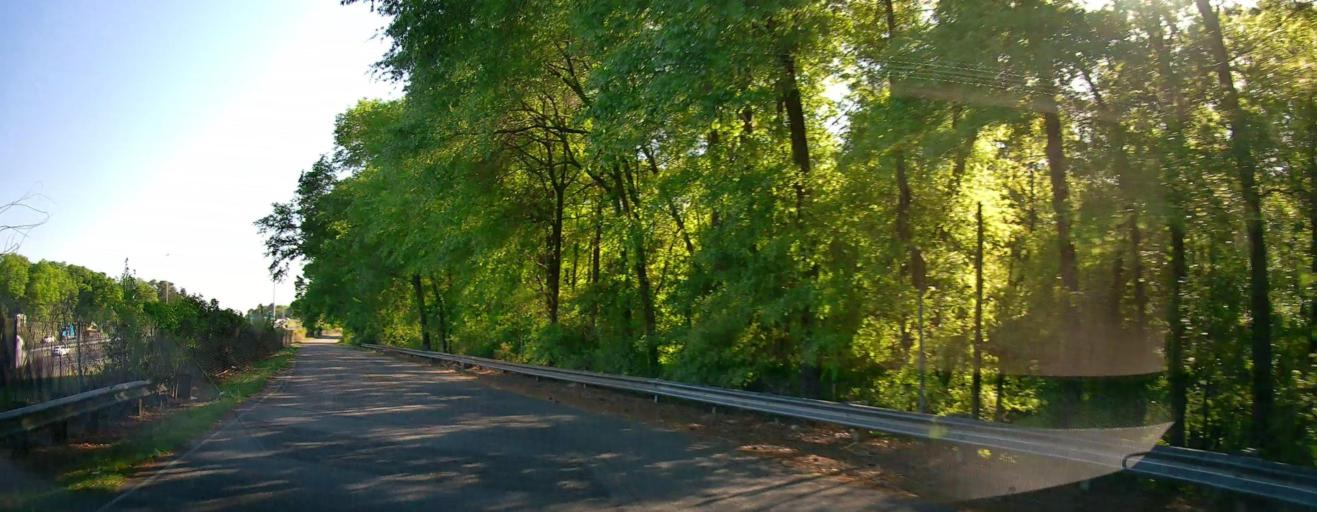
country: US
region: Georgia
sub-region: Houston County
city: Perry
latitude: 32.4553
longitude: -83.7531
